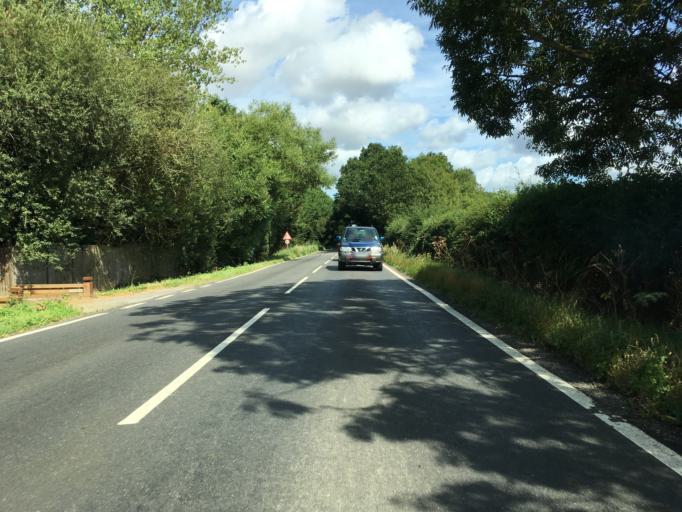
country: GB
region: England
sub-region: Kent
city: Staplehurst
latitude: 51.1433
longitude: 0.5519
